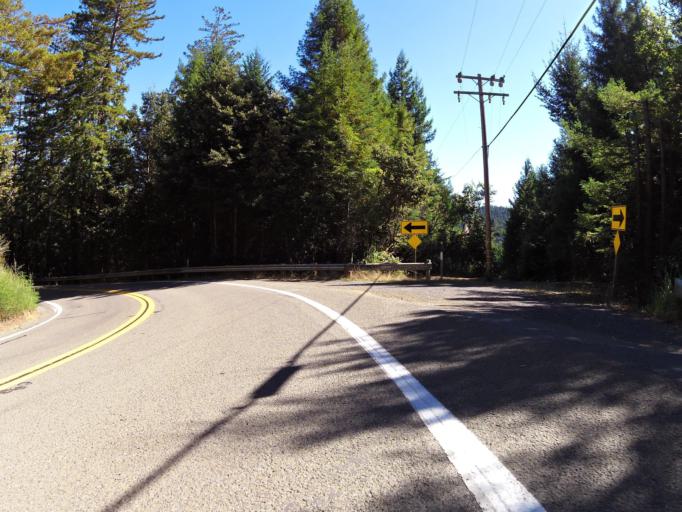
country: US
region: California
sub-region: Mendocino County
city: Fort Bragg
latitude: 39.7206
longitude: -123.8051
